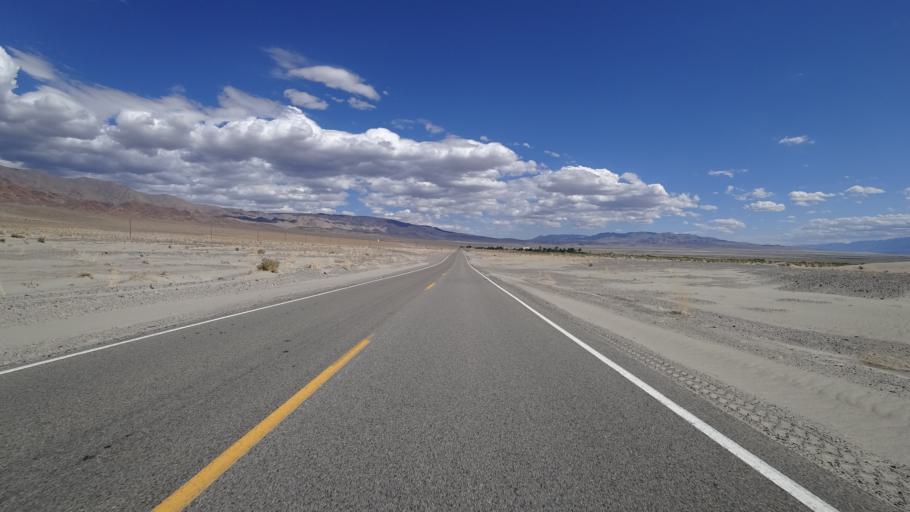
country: US
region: California
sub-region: Inyo County
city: Lone Pine
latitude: 36.4998
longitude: -117.8821
